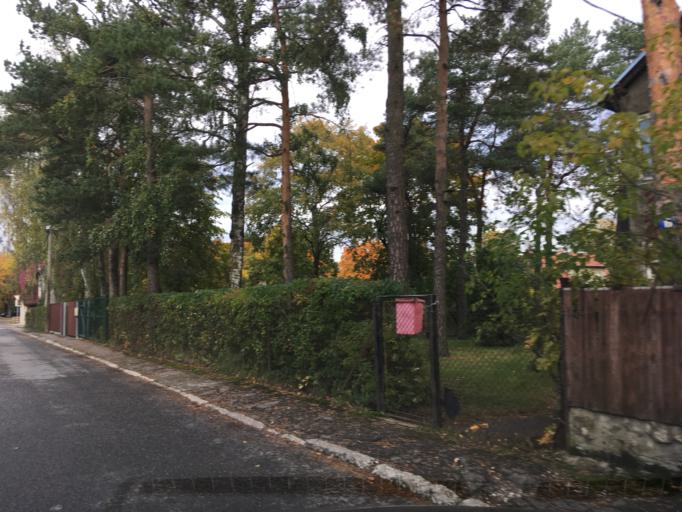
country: EE
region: Harju
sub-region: Saue vald
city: Laagri
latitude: 59.3781
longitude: 24.6560
